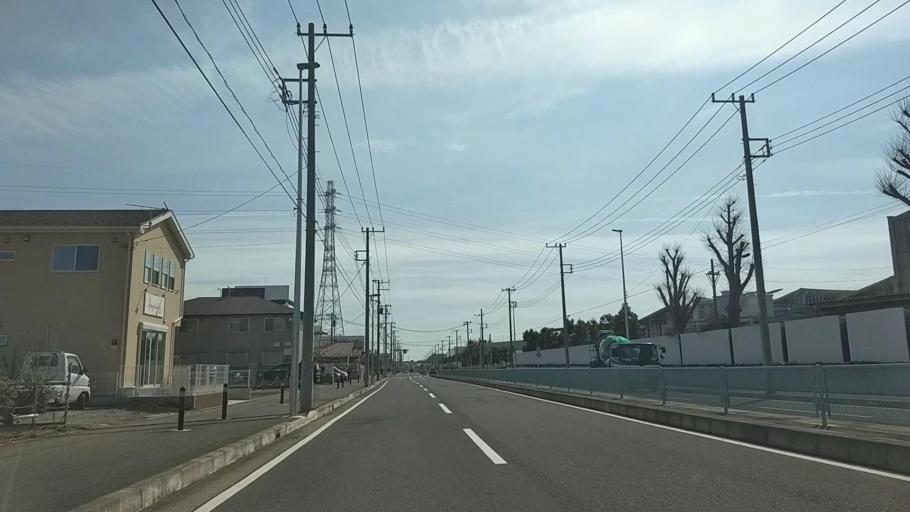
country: JP
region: Kanagawa
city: Fujisawa
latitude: 35.4014
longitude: 139.4556
